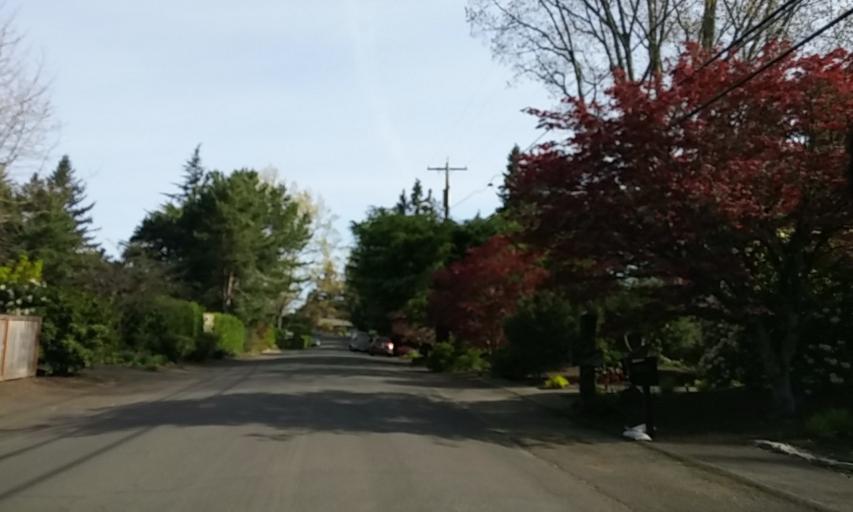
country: US
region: Oregon
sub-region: Washington County
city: West Slope
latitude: 45.4996
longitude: -122.7753
